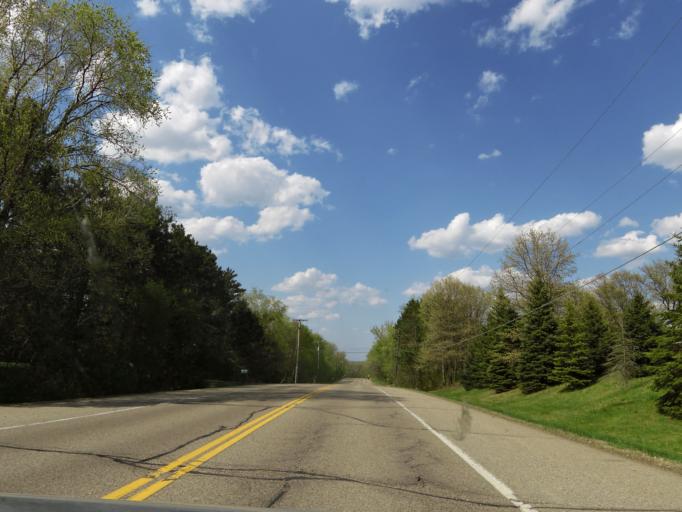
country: US
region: Minnesota
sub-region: Washington County
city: Oak Park Heights
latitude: 45.0026
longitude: -92.8225
